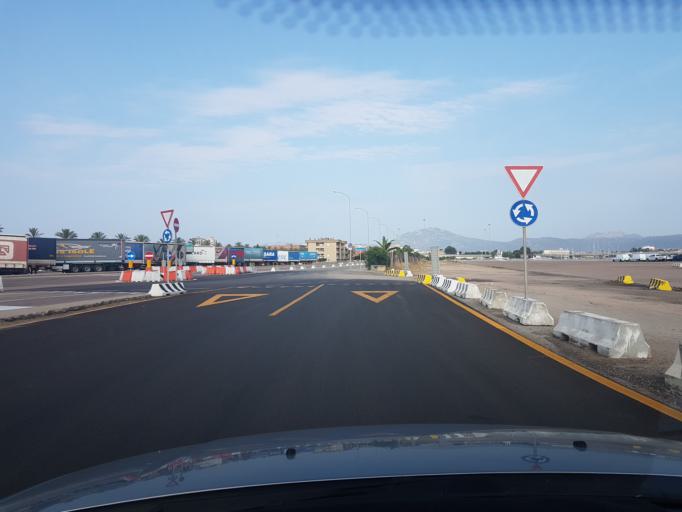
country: IT
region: Sardinia
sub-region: Provincia di Olbia-Tempio
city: Olbia
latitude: 40.9242
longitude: 9.5153
